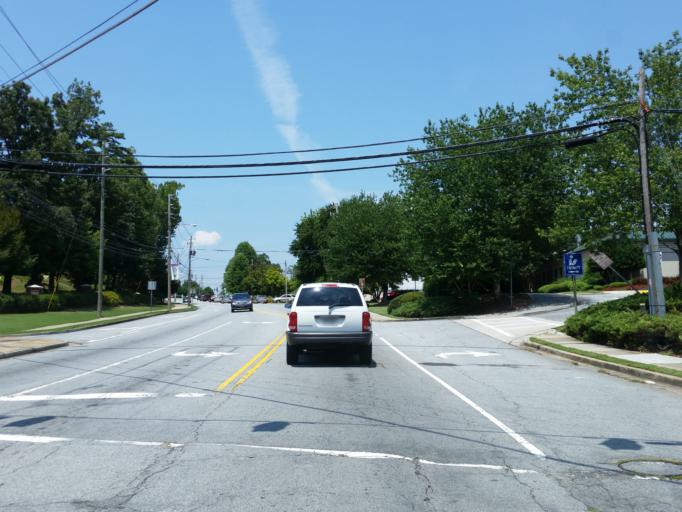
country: US
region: Georgia
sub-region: DeKalb County
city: Dunwoody
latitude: 33.9437
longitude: -84.3317
